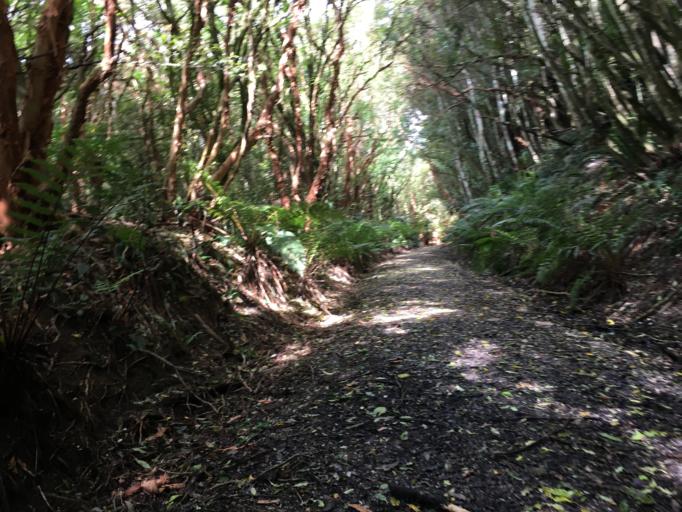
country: NZ
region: Otago
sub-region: Clutha District
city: Papatowai
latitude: -46.4965
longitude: 169.4796
